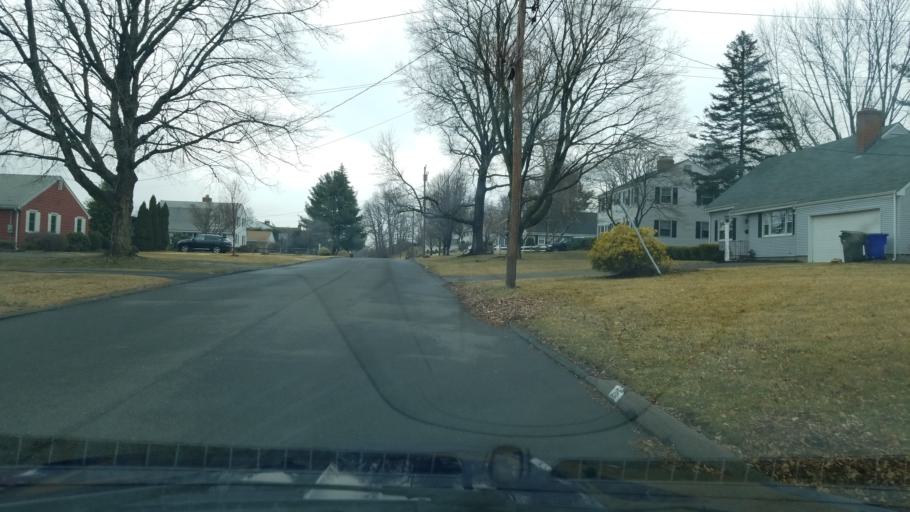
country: US
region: Connecticut
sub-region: Hartford County
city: Wethersfield
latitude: 41.6829
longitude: -72.6679
